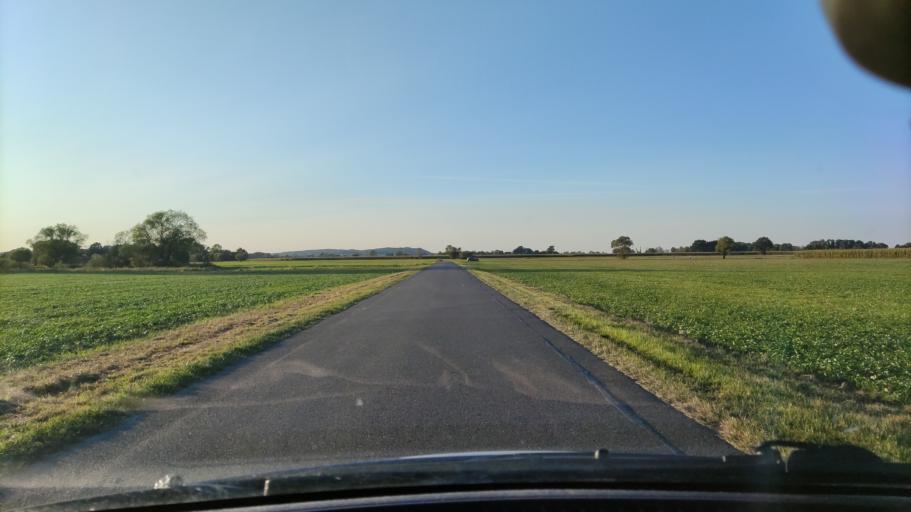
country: DE
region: Lower Saxony
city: Dannenberg
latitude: 53.1265
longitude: 11.0944
